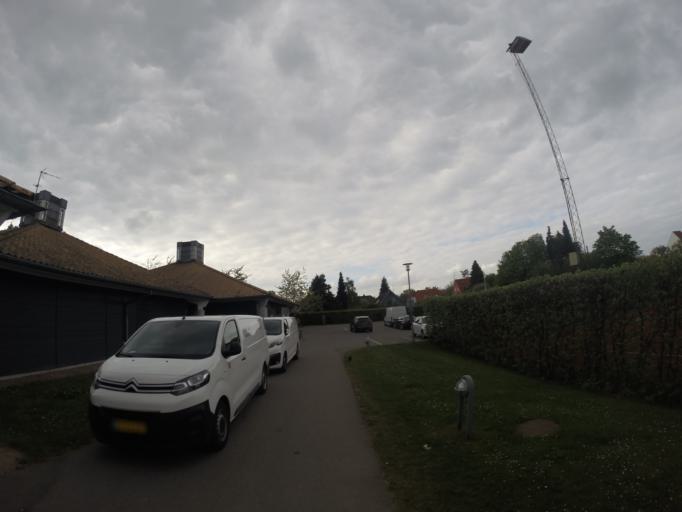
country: DK
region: Capital Region
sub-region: Hoje-Taastrup Kommune
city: Flong
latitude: 55.6490
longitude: 12.2055
